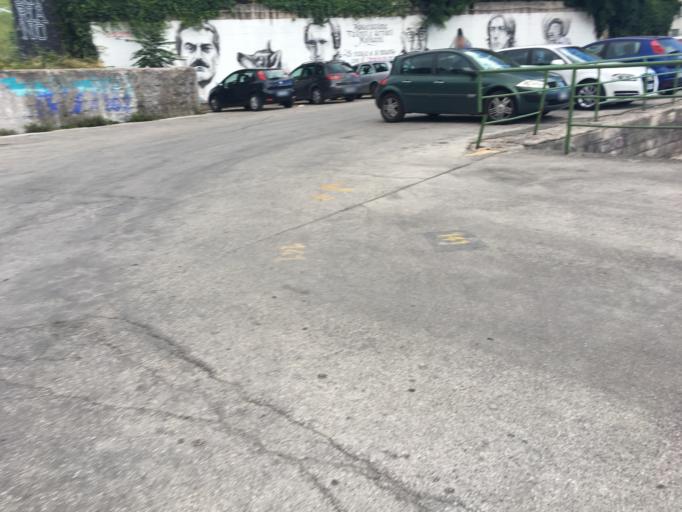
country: IT
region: Molise
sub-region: Provincia di Campobasso
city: Campobasso
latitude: 41.5549
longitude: 14.6590
